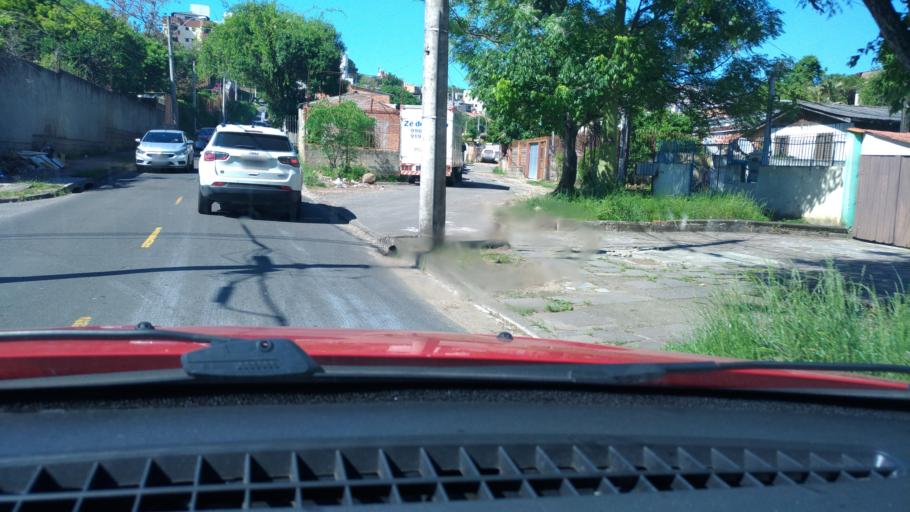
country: BR
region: Rio Grande do Sul
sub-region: Porto Alegre
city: Porto Alegre
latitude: -30.0313
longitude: -51.1477
